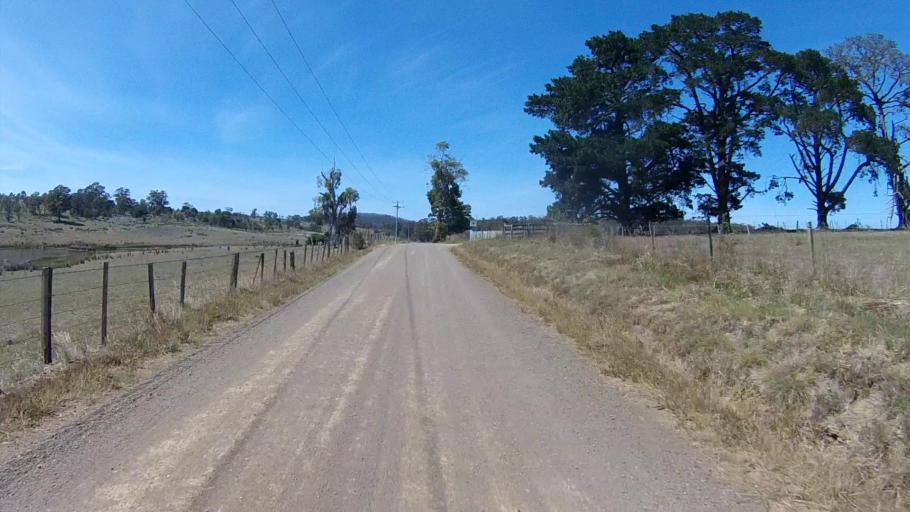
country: AU
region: Tasmania
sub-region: Sorell
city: Sorell
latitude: -42.7753
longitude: 147.6529
